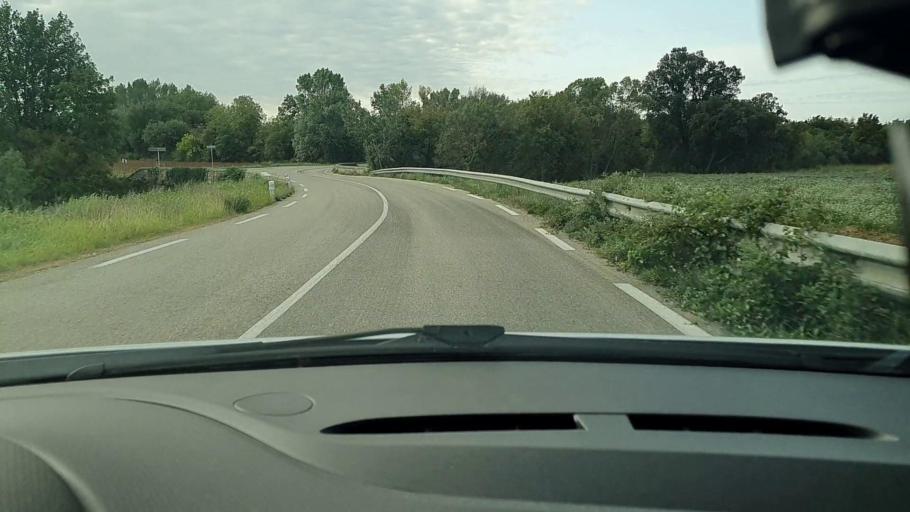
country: FR
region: Languedoc-Roussillon
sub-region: Departement du Gard
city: Mons
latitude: 44.0895
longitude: 4.2194
